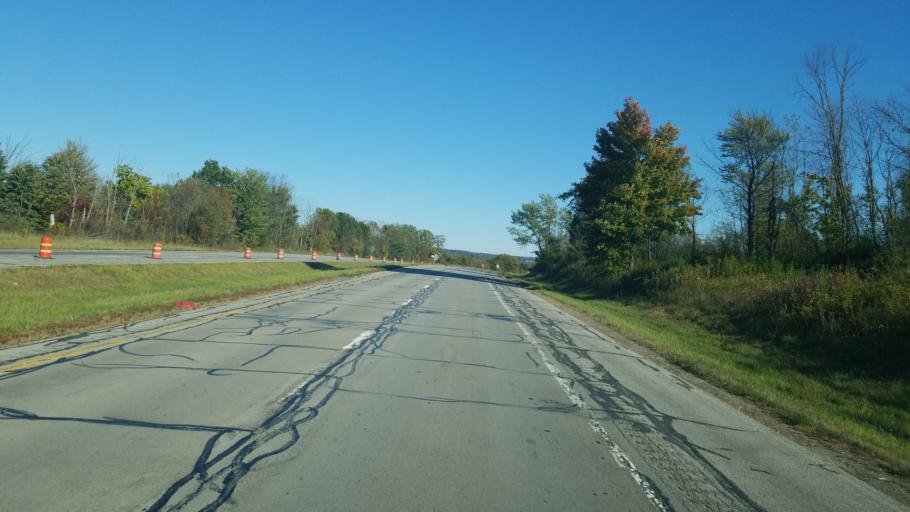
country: US
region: Ohio
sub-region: Medina County
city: Westfield Center
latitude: 41.0390
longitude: -81.9319
